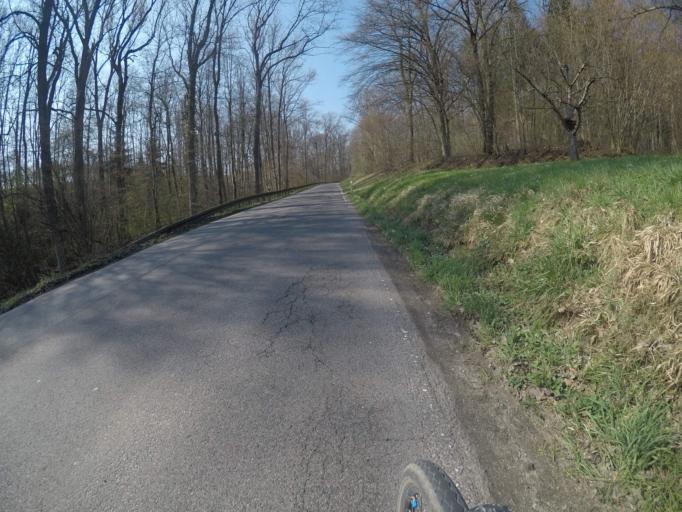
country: DE
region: Baden-Wuerttemberg
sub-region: Regierungsbezirk Stuttgart
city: Neckartenzlingen
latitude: 48.5807
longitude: 9.2290
